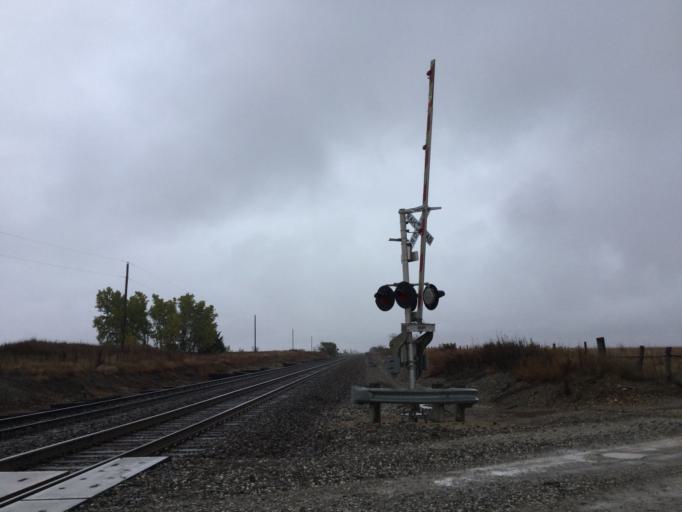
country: US
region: Kansas
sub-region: Butler County
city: El Dorado
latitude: 37.9849
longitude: -96.6857
